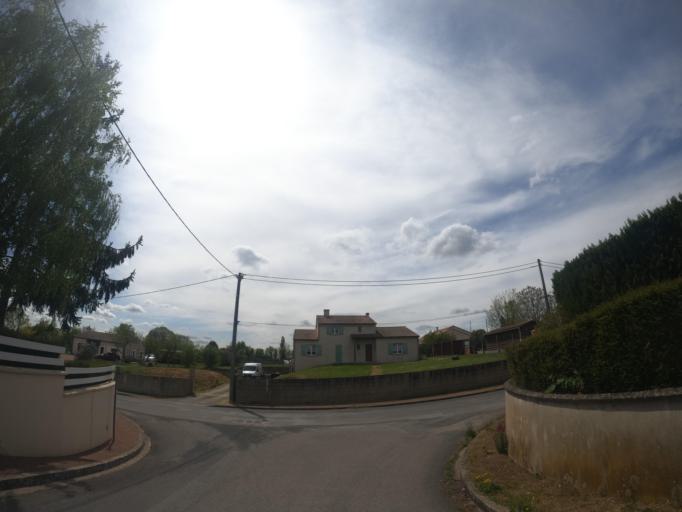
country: FR
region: Poitou-Charentes
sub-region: Departement des Deux-Sevres
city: Saint-Jean-de-Thouars
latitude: 46.9243
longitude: -0.1961
